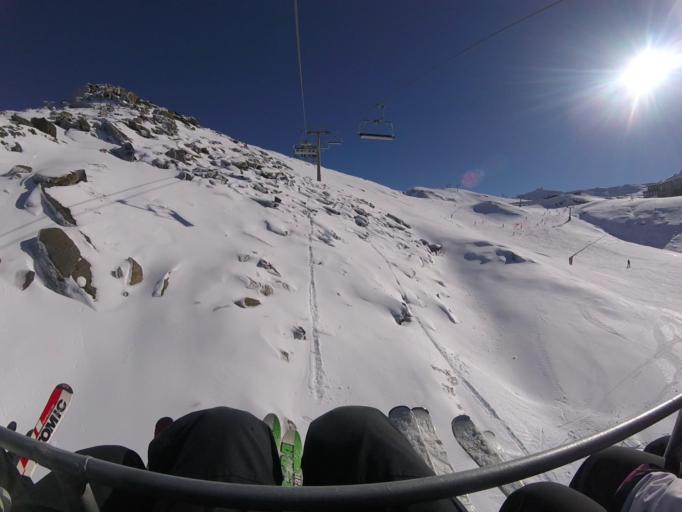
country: ES
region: Andalusia
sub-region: Provincia de Granada
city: Guejar-Sierra
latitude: 37.0748
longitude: -3.3867
